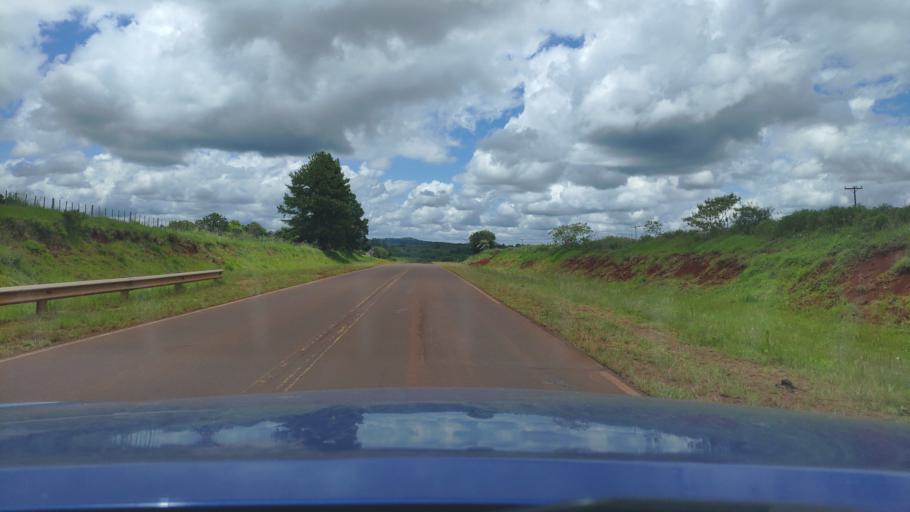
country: AR
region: Misiones
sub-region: Departamento de San Javier
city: San Javier
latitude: -27.8426
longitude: -55.2390
